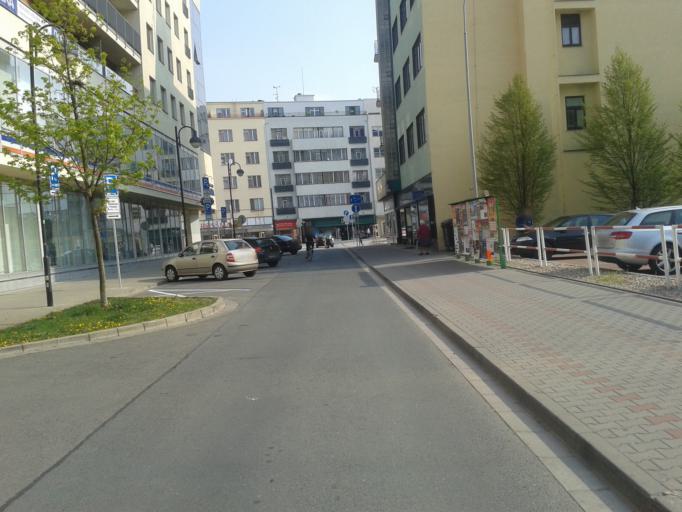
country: CZ
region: Pardubicky
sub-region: Okres Pardubice
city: Pardubice
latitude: 50.0373
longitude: 15.7714
